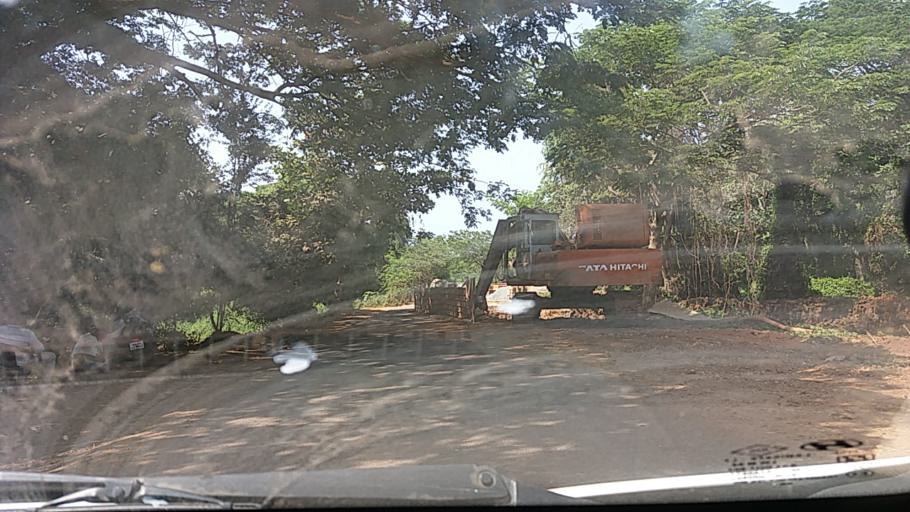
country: IN
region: Goa
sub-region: South Goa
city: Madgaon
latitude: 15.2788
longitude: 73.9533
